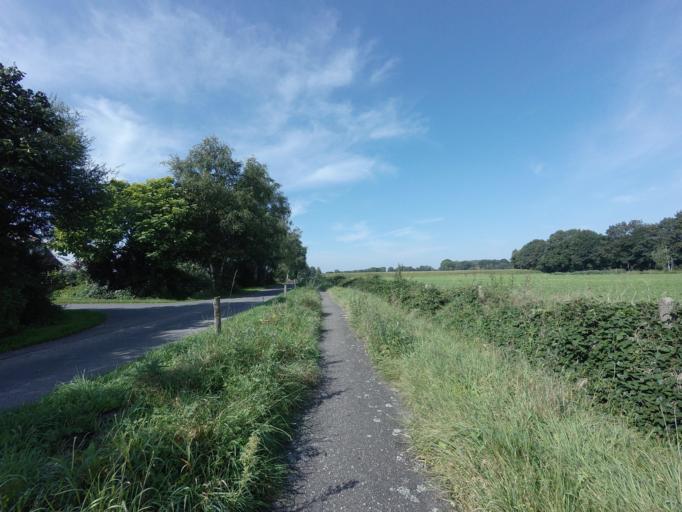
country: NL
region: Overijssel
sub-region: Gemeente Enschede
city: Enschede
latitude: 52.1860
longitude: 6.9264
